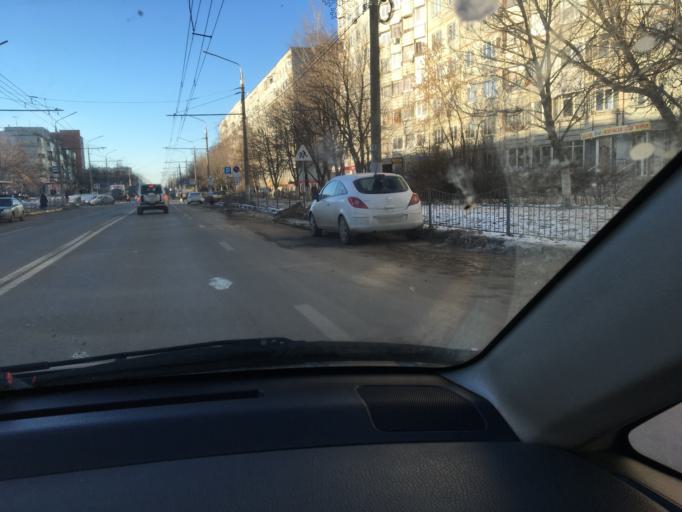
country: RU
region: Tula
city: Tula
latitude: 54.2186
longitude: 37.6206
